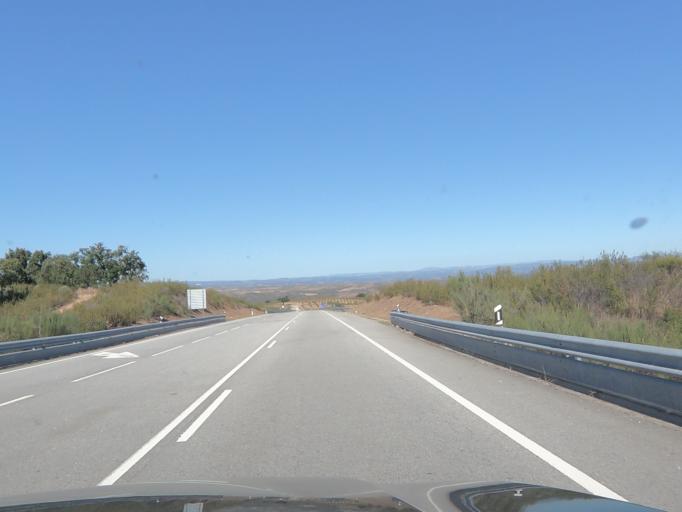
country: PT
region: Braganca
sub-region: Mirandela
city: Mirandela
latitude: 41.4822
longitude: -7.2245
